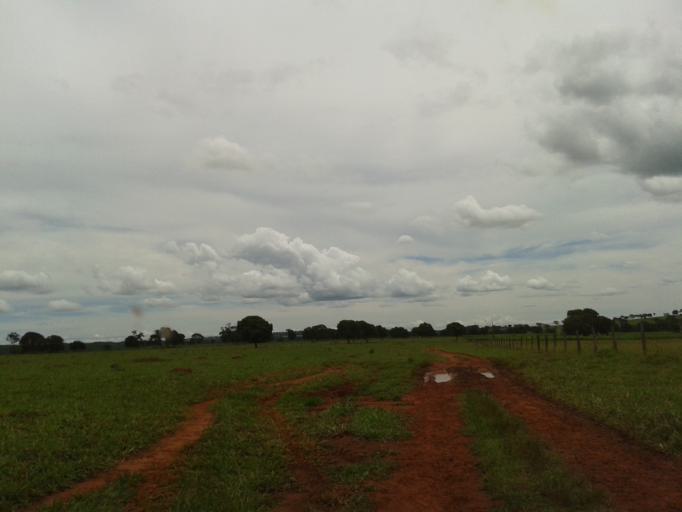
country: BR
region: Minas Gerais
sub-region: Santa Vitoria
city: Santa Vitoria
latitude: -18.7882
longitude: -49.8541
